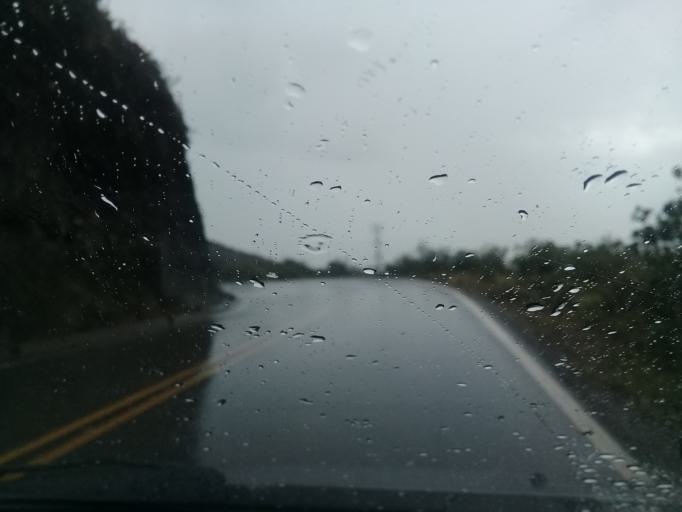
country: CO
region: Cundinamarca
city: Guasca
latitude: 4.8454
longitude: -73.8184
